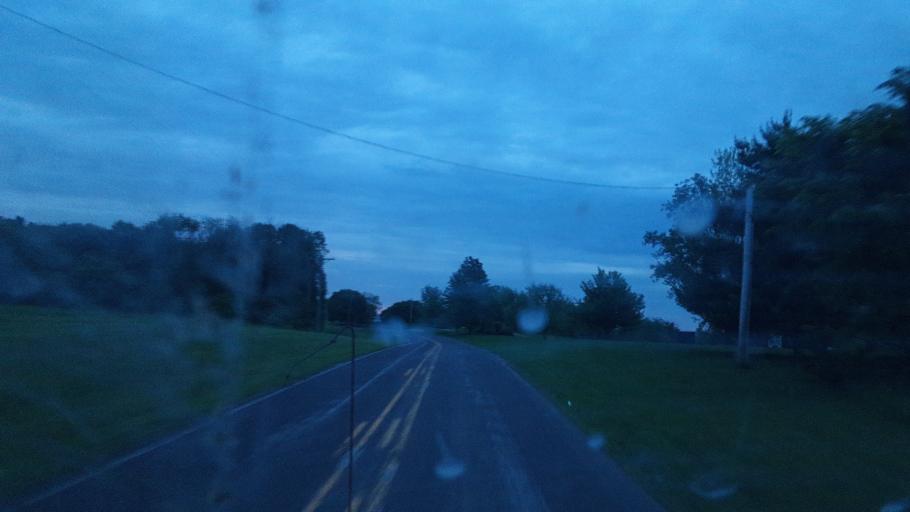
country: US
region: Missouri
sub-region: Clark County
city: Kahoka
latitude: 40.4352
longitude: -91.5906
